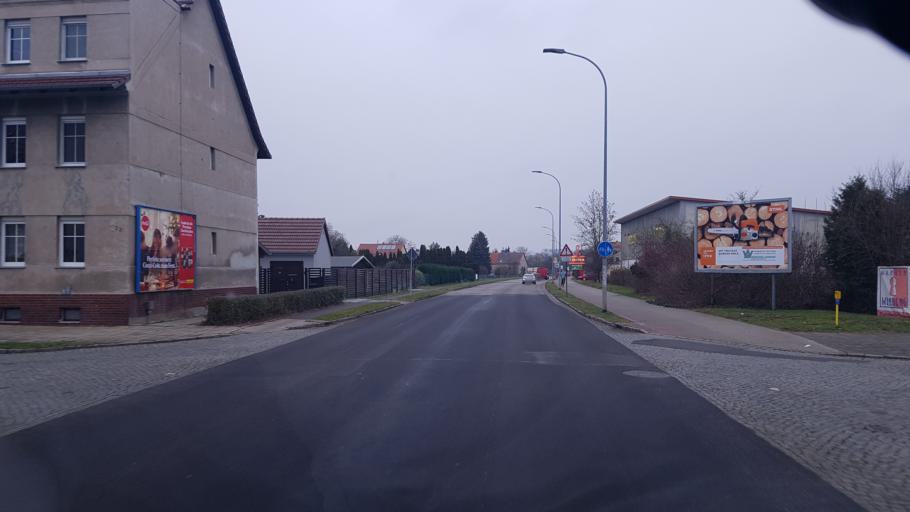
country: DE
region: Brandenburg
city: Guben
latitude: 51.9500
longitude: 14.7028
